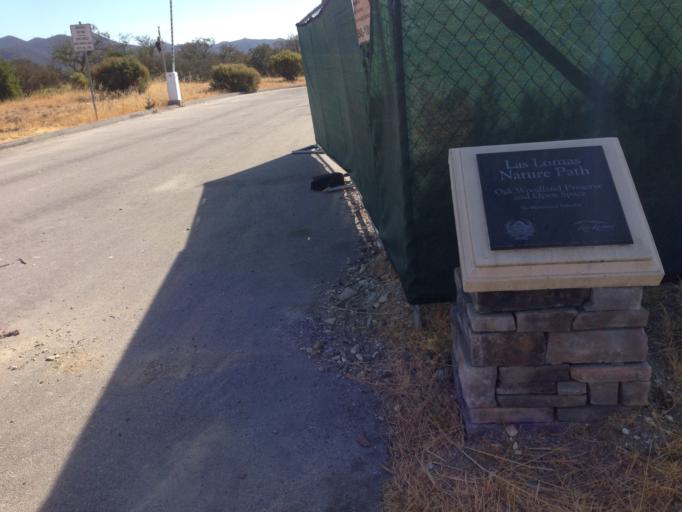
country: US
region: California
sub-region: San Luis Obispo County
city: Atascadero
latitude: 35.4536
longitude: -120.6269
